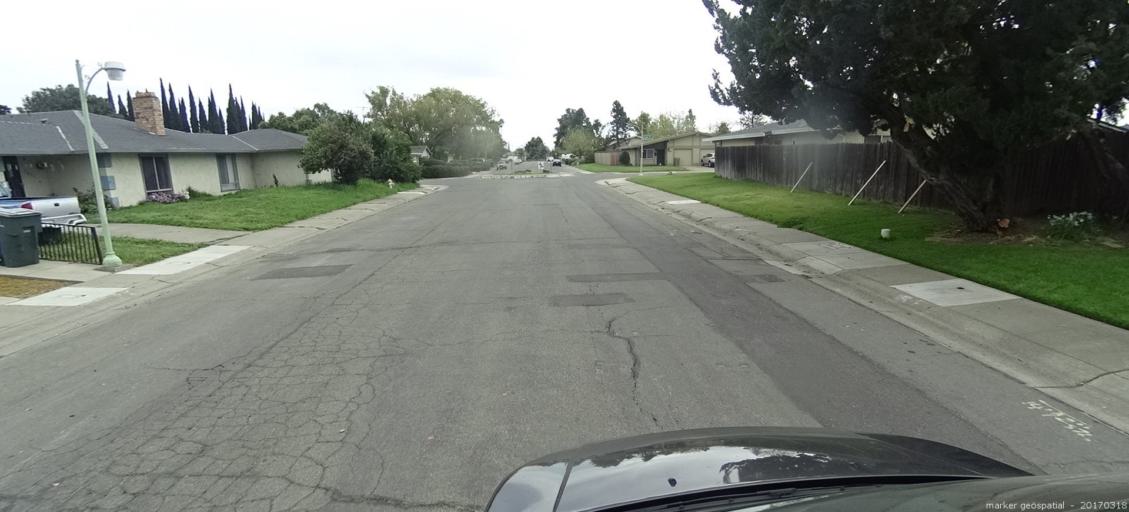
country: US
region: California
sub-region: Sacramento County
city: Parkway
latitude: 38.4805
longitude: -121.4353
